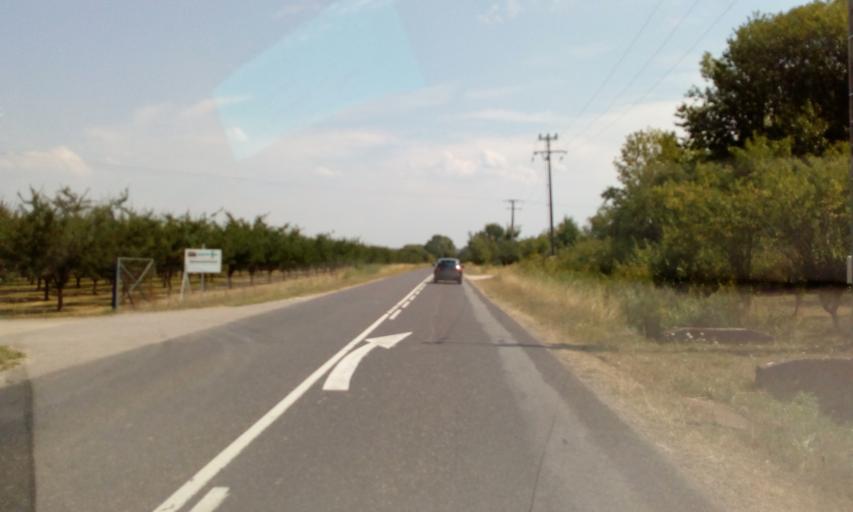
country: FR
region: Lorraine
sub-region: Departement de la Meuse
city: Vigneulles-les-Hattonchatel
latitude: 48.9979
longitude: 5.7064
